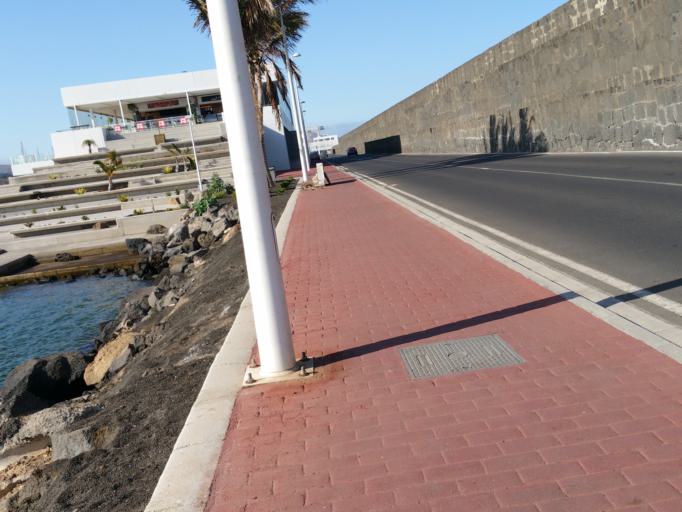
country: ES
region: Canary Islands
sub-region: Provincia de Las Palmas
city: Arrecife
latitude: 28.9602
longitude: -13.5399
